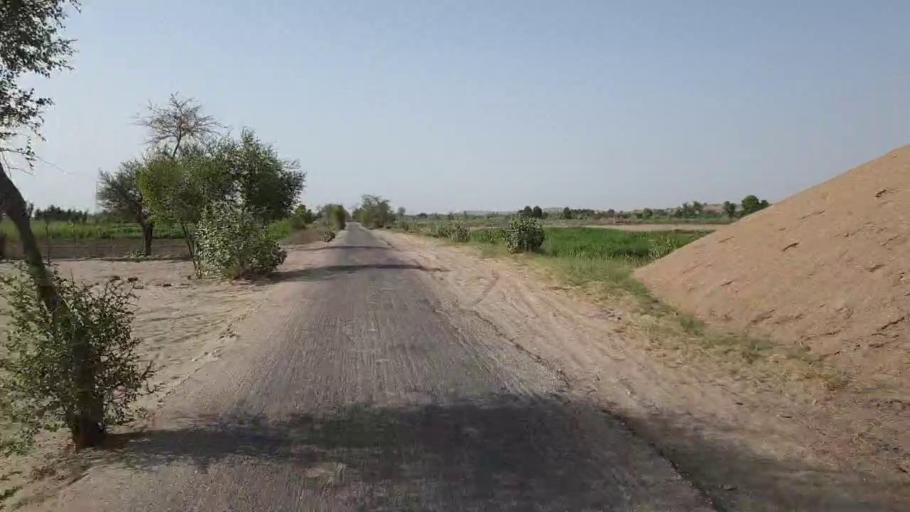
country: PK
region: Sindh
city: Kandiari
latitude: 26.7012
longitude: 68.9645
